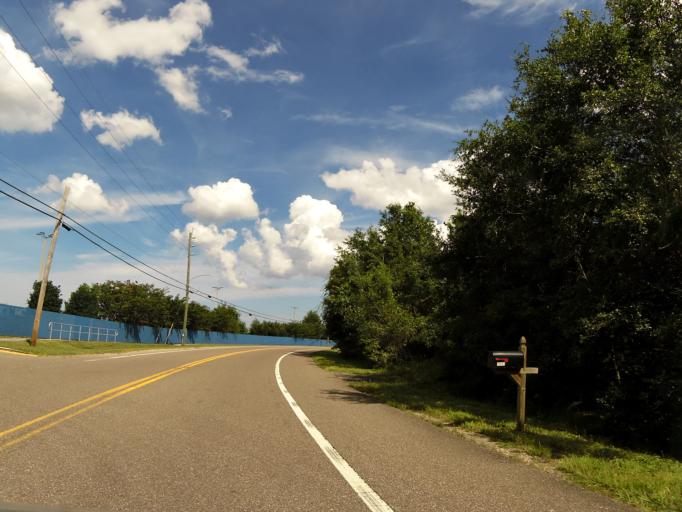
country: US
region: Florida
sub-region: Duval County
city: Jacksonville
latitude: 30.4244
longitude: -81.5760
